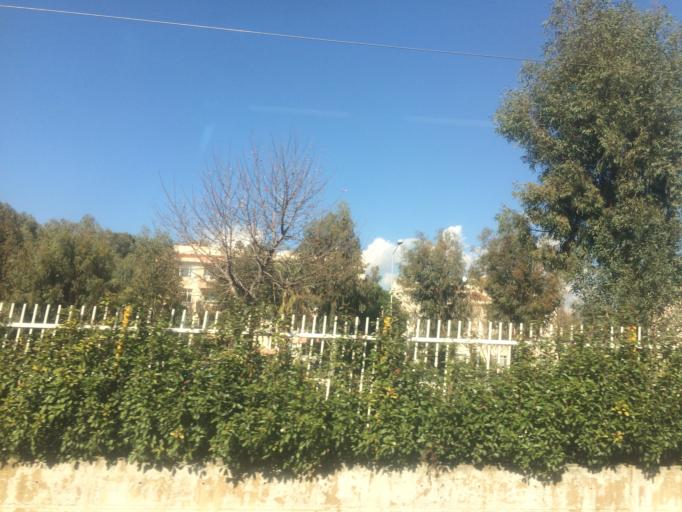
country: TR
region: Izmir
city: Karsiyaka
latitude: 38.4658
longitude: 27.1452
